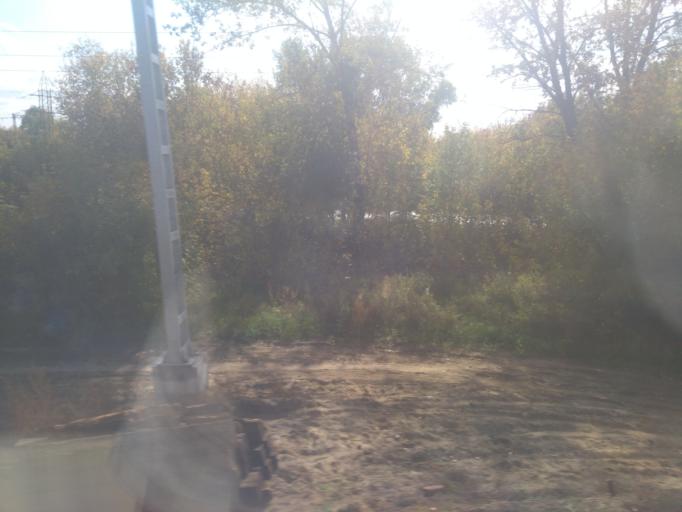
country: RU
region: Tatarstan
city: Staroye Arakchino
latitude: 55.8018
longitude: 49.0039
